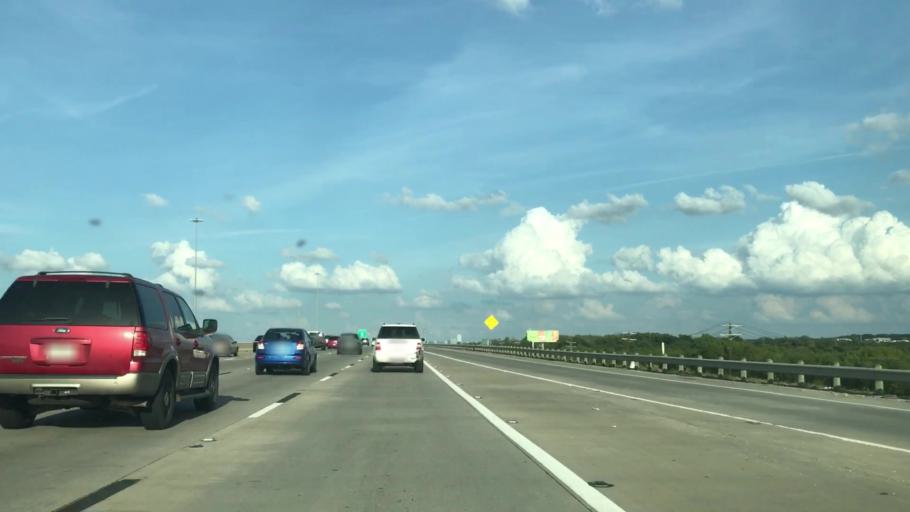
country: US
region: Texas
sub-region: Dallas County
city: Irving
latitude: 32.7633
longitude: -96.9405
